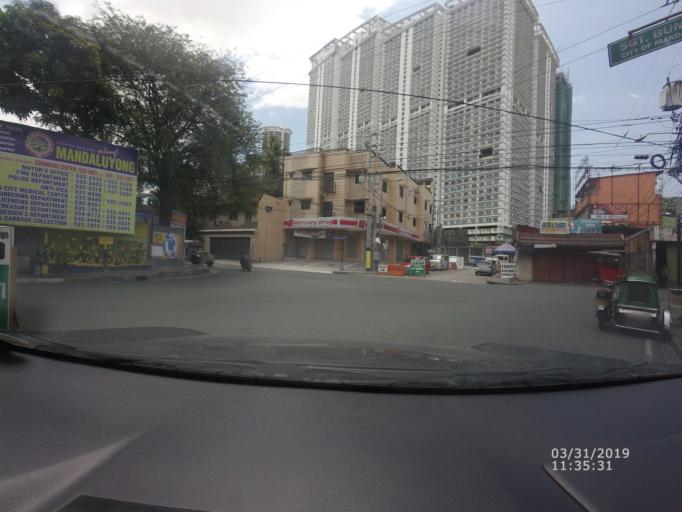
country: PH
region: Metro Manila
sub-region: Mandaluyong
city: Mandaluyong City
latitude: 14.5699
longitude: 121.0363
